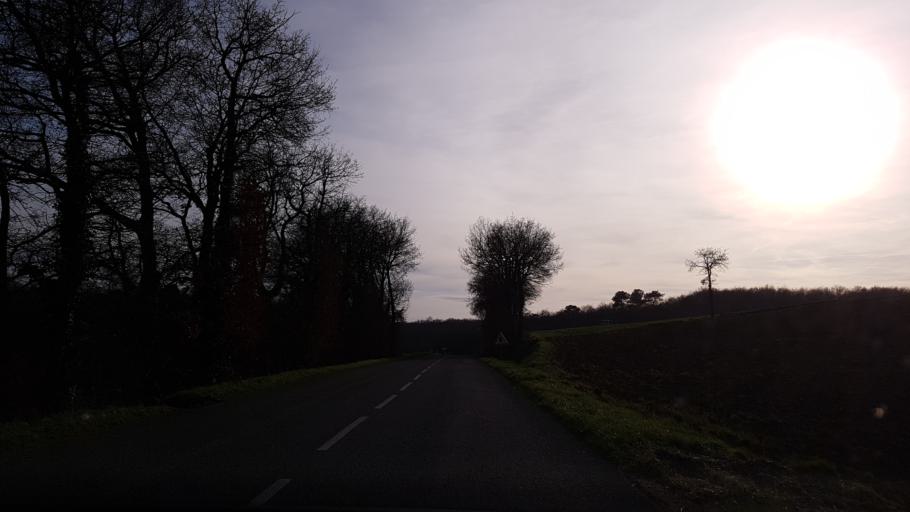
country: FR
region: Languedoc-Roussillon
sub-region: Departement de l'Aude
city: Villeneuve-la-Comptal
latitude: 43.2217
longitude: 1.9169
